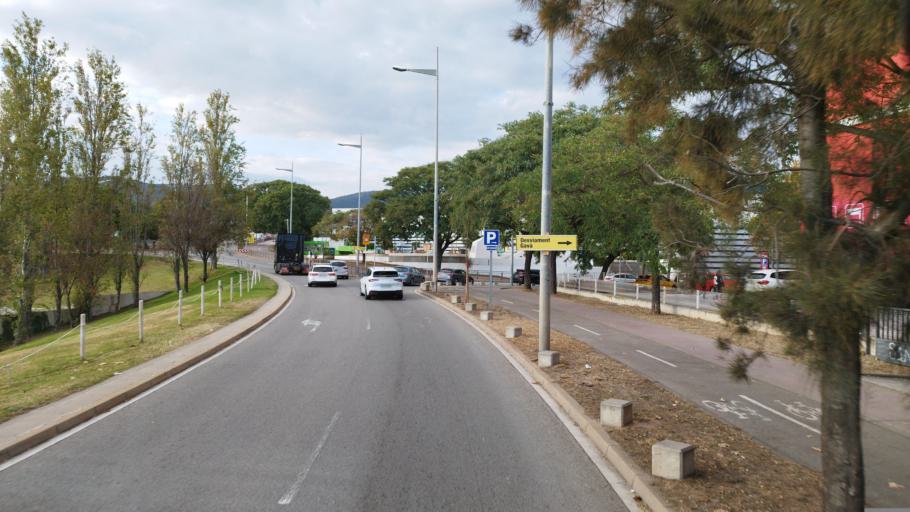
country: ES
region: Catalonia
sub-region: Provincia de Barcelona
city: Castelldefels
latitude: 41.2821
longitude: 1.9879
